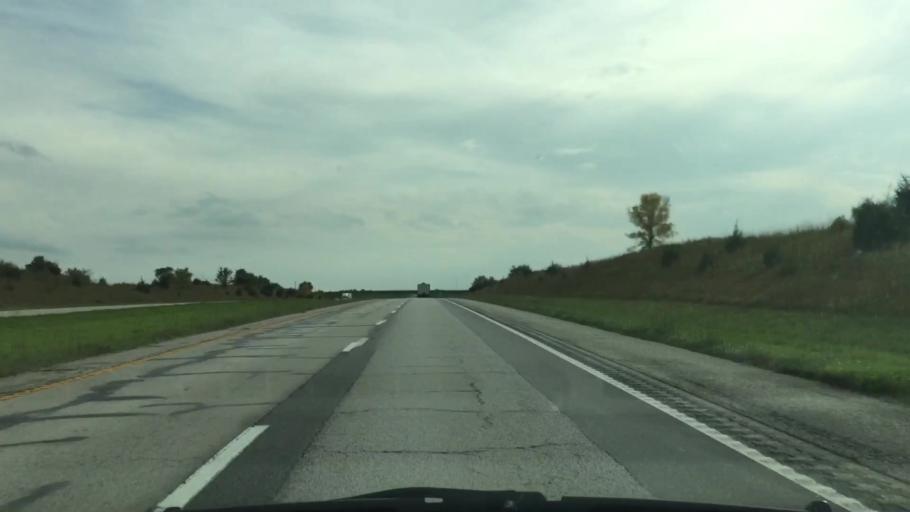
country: US
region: Missouri
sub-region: Harrison County
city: Bethany
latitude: 40.4224
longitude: -93.9896
